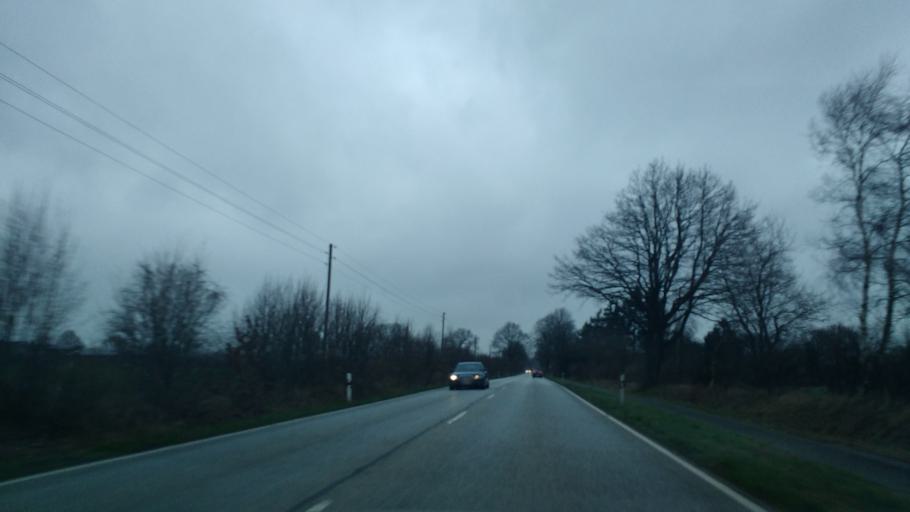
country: DE
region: Schleswig-Holstein
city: Peissen
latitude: 54.0175
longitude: 9.5911
